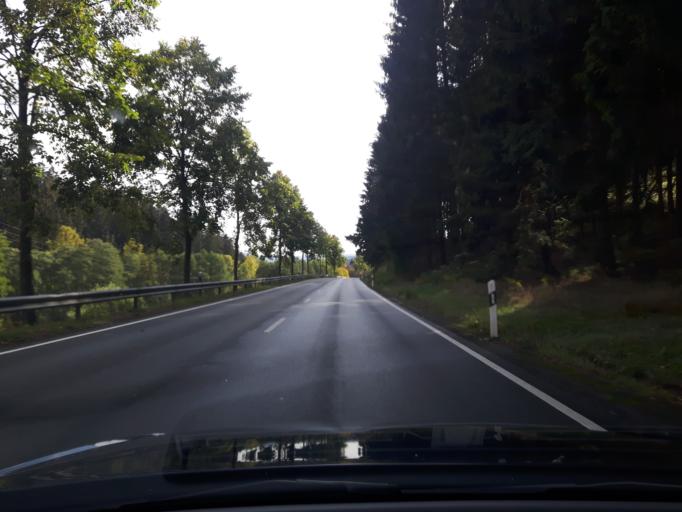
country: DE
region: North Rhine-Westphalia
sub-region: Regierungsbezirk Arnsberg
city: Bad Berleburg
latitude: 51.0324
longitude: 8.4074
